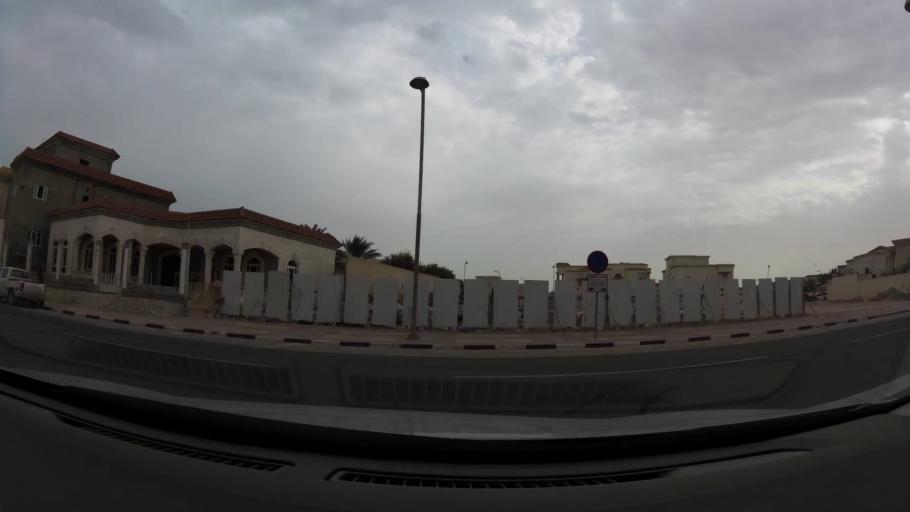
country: QA
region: Baladiyat ad Dawhah
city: Doha
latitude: 25.3413
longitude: 51.4840
